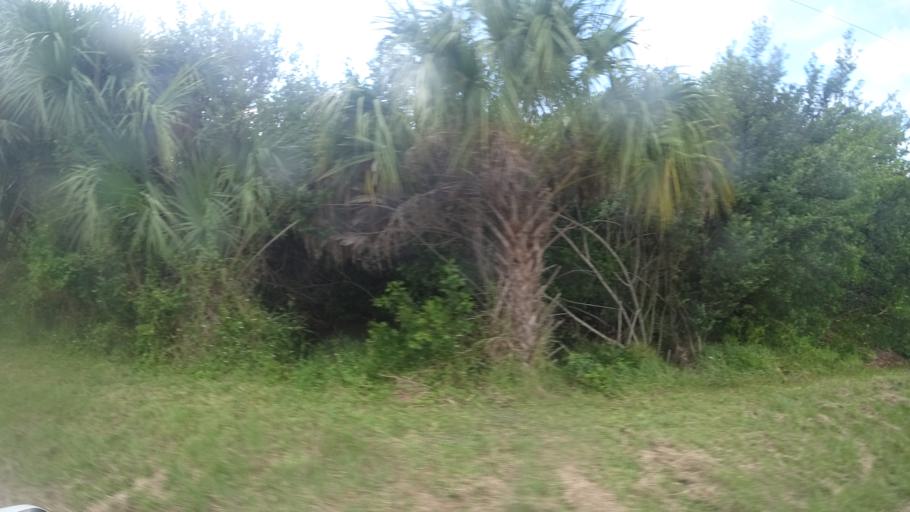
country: US
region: Florida
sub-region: Manatee County
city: Memphis
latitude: 27.5886
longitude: -82.5565
